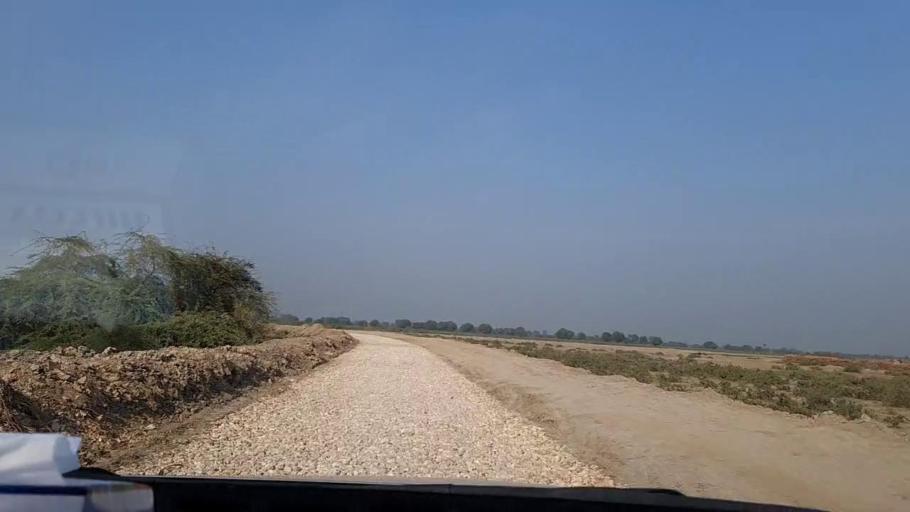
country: PK
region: Sindh
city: Tando Ghulam Ali
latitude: 25.1593
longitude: 68.8787
